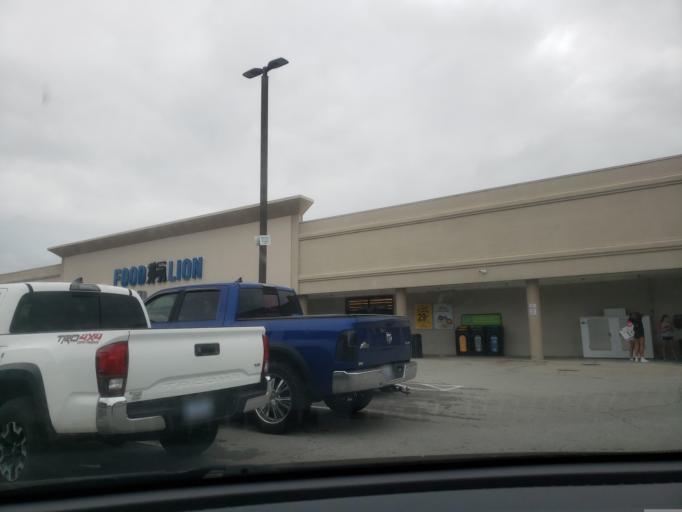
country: US
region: North Carolina
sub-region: Onslow County
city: Sneads Ferry
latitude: 34.5267
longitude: -77.4372
